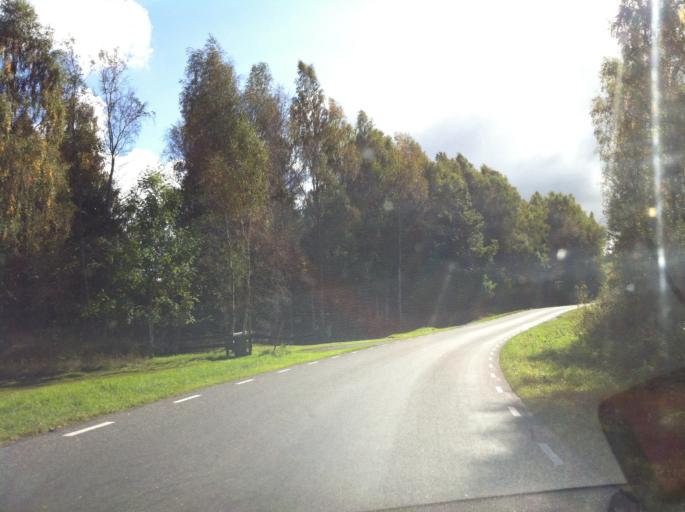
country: SE
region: Skane
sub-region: Kristianstads Kommun
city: Degeberga
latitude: 55.7415
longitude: 13.9385
